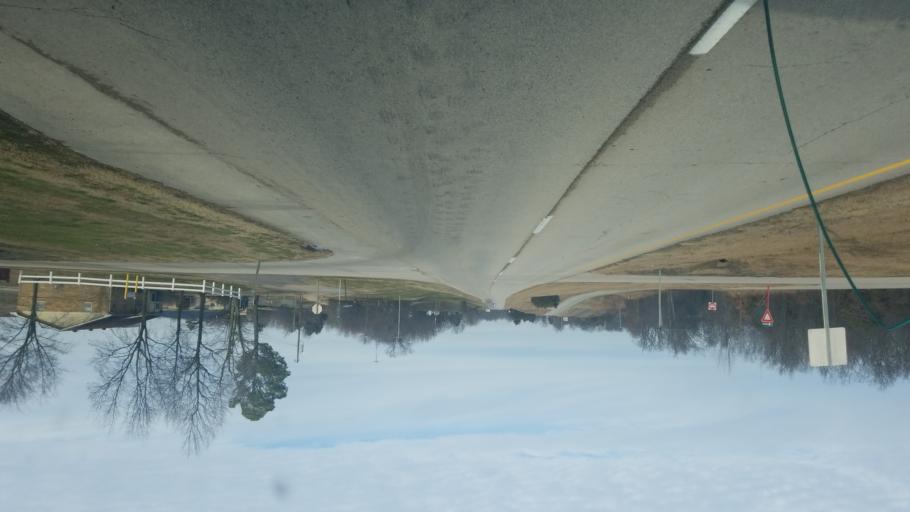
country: US
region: Missouri
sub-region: Stoddard County
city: Dexter
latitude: 36.8331
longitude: -89.9413
